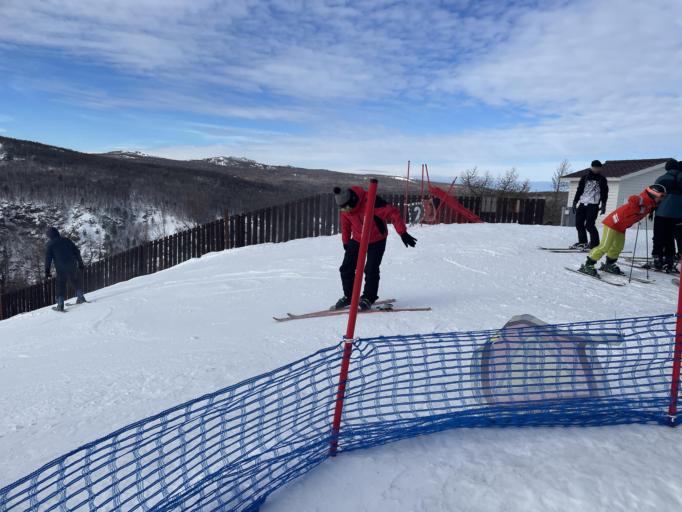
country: RU
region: Bashkortostan
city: Abzakovo
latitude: 53.5913
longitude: 58.5576
